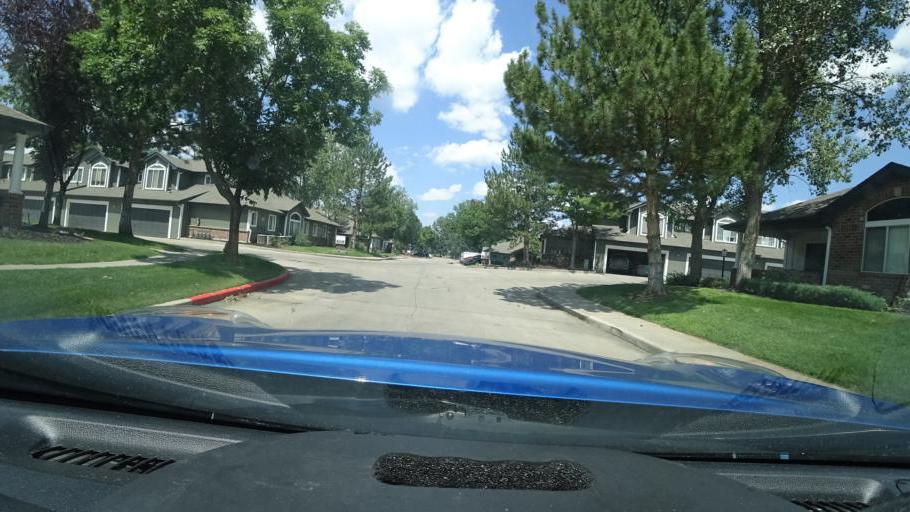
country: US
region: Colorado
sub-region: Arapahoe County
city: Glendale
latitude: 39.7001
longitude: -104.8884
